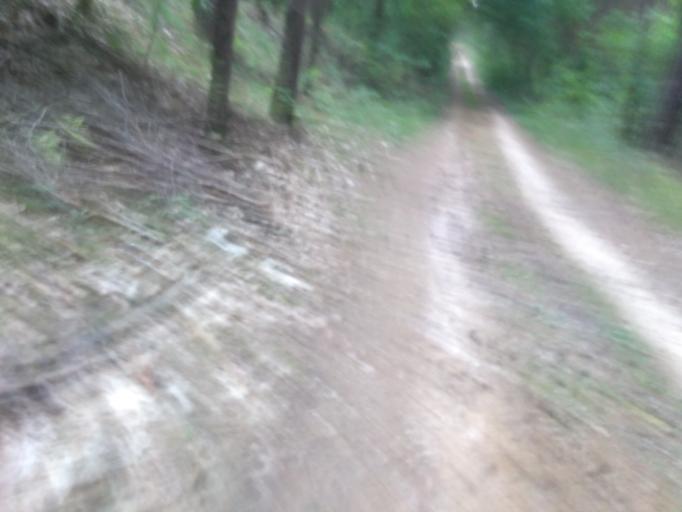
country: DE
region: Brandenburg
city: Elsterwerda
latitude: 51.4809
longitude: 13.5199
